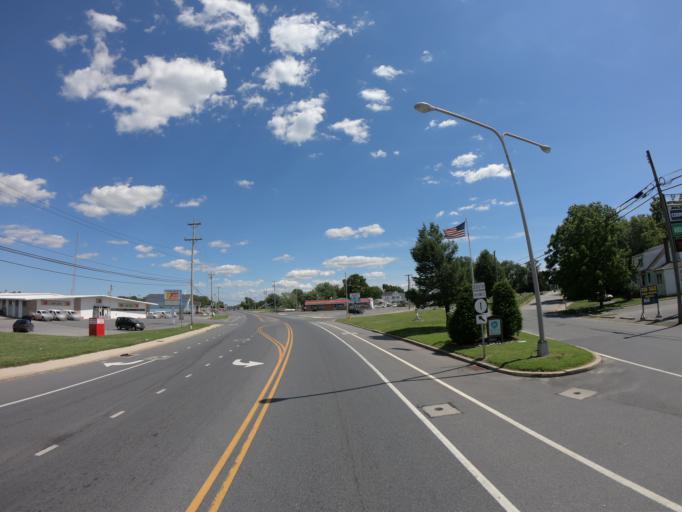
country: US
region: Delaware
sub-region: Sussex County
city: Milford
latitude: 38.9273
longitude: -75.4290
